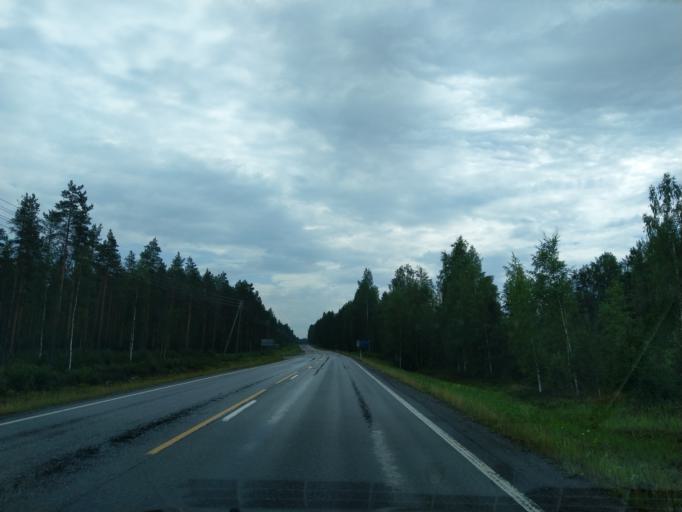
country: FI
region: Southern Savonia
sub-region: Savonlinna
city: Punkaharju
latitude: 61.6589
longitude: 29.4174
